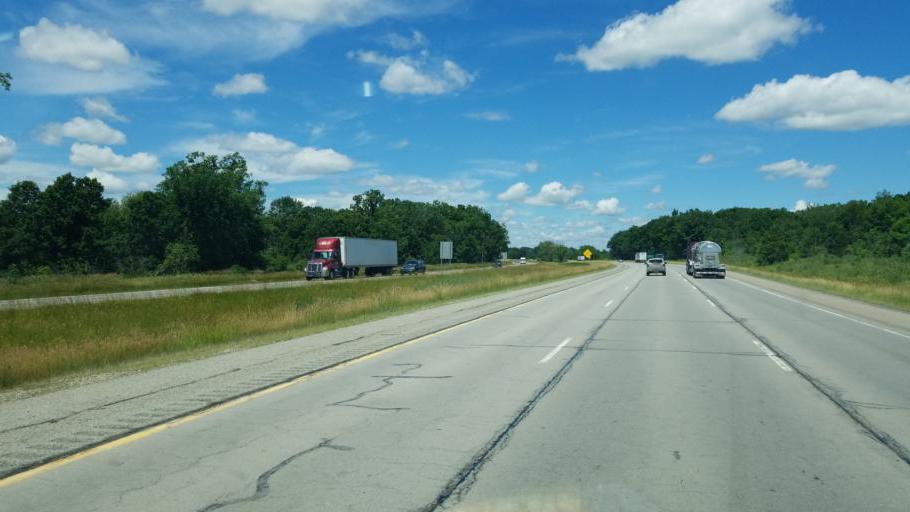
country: US
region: Michigan
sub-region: Livingston County
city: Howell
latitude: 42.6234
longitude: -84.0007
